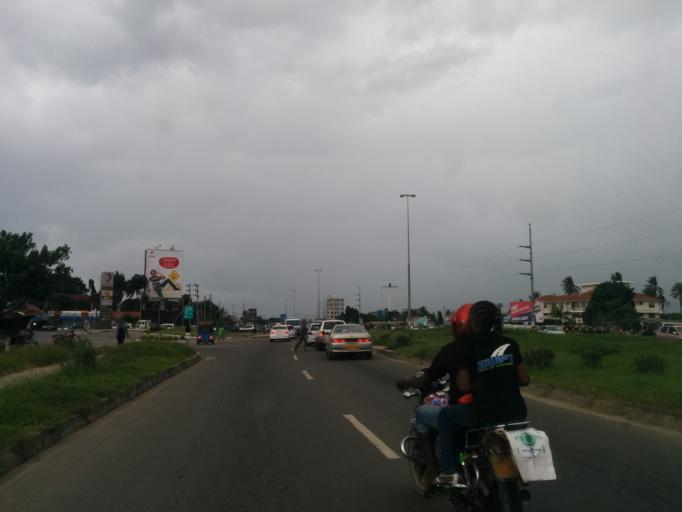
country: TZ
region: Dar es Salaam
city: Magomeni
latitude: -6.7732
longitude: 39.2214
